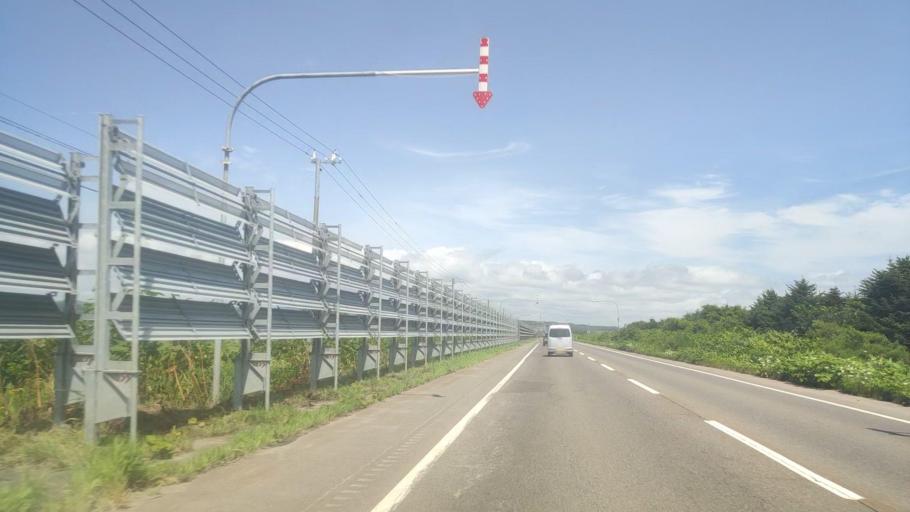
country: JP
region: Hokkaido
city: Nanae
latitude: 42.2973
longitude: 140.2718
